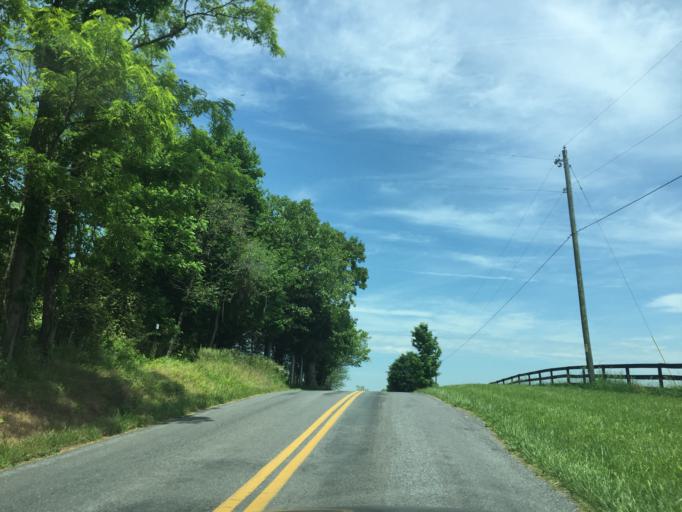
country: US
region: Virginia
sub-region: Warren County
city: Shenandoah Farms
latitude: 38.9737
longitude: -78.1244
